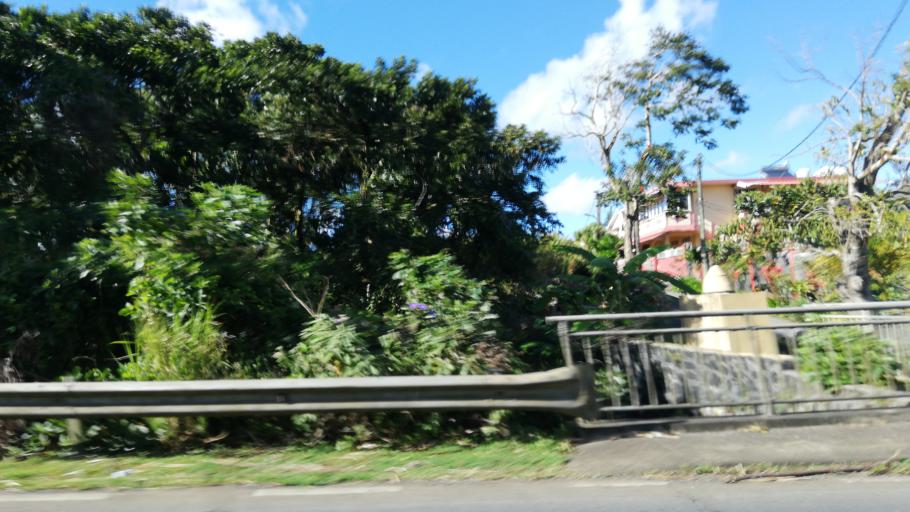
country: MU
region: Moka
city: La Dagotiere
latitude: -20.2325
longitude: 57.5573
